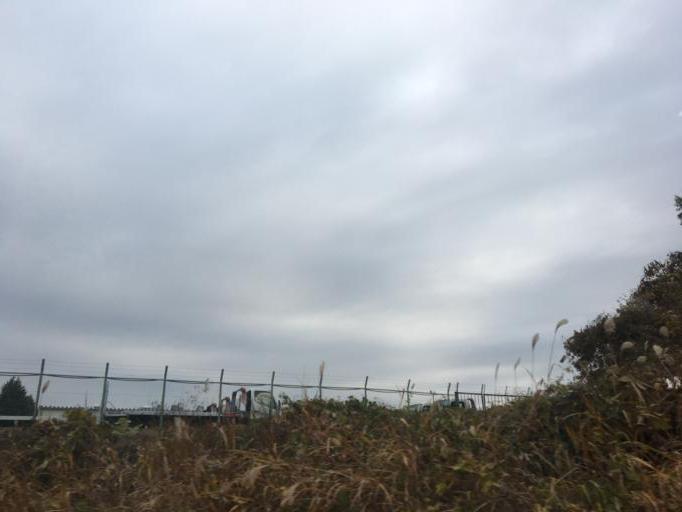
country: JP
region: Tochigi
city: Oyama
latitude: 36.3342
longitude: 139.8054
